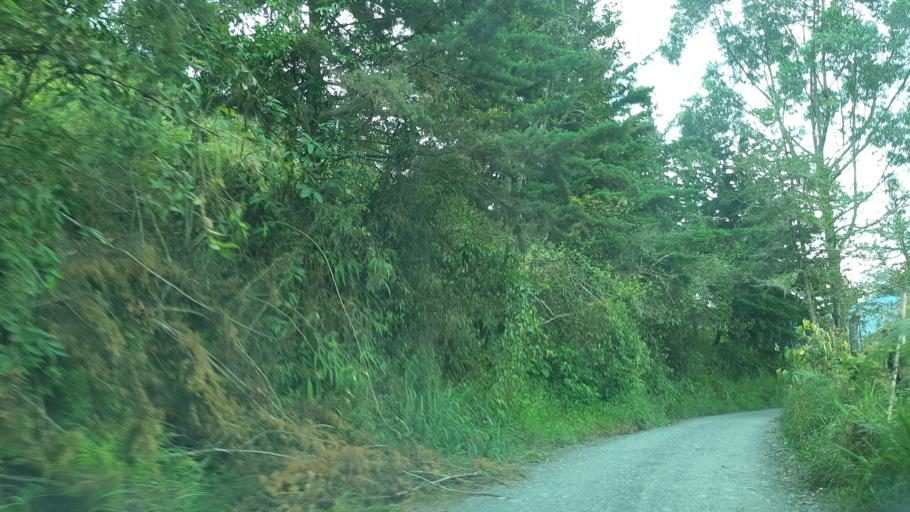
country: CO
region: Boyaca
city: Garagoa
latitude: 4.9828
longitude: -73.3221
